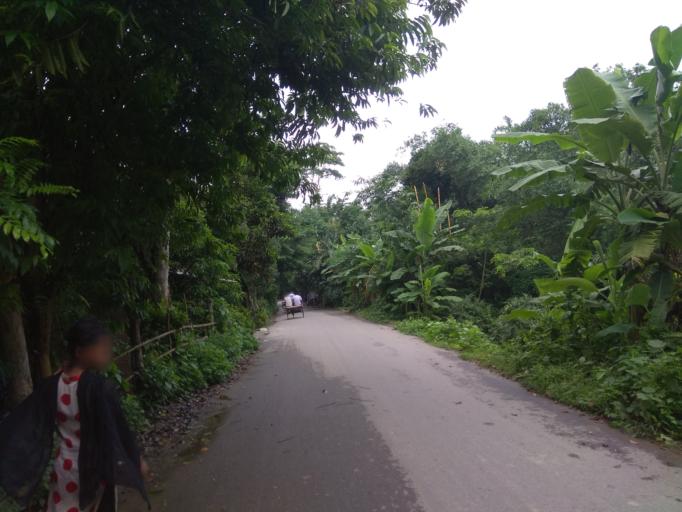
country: BD
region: Dhaka
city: Dohar
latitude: 23.4305
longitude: 90.0717
